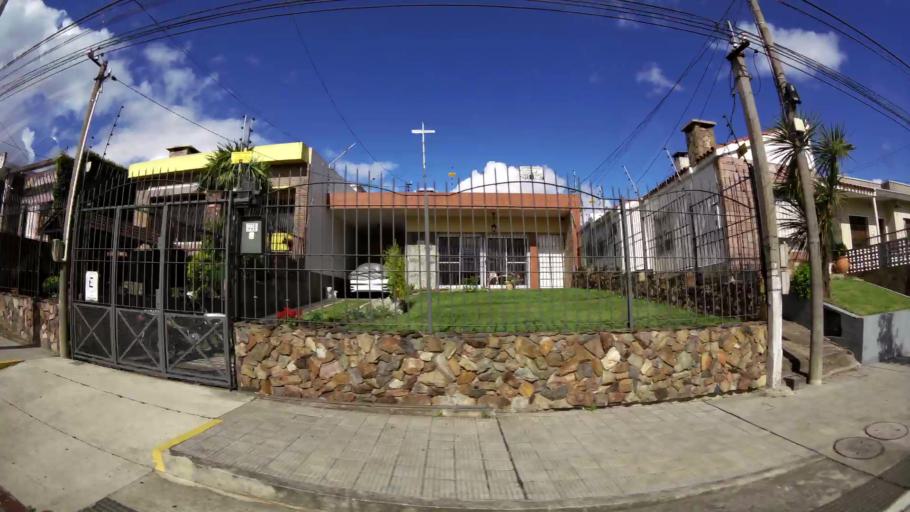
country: UY
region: Canelones
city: La Paz
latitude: -34.8229
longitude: -56.2198
